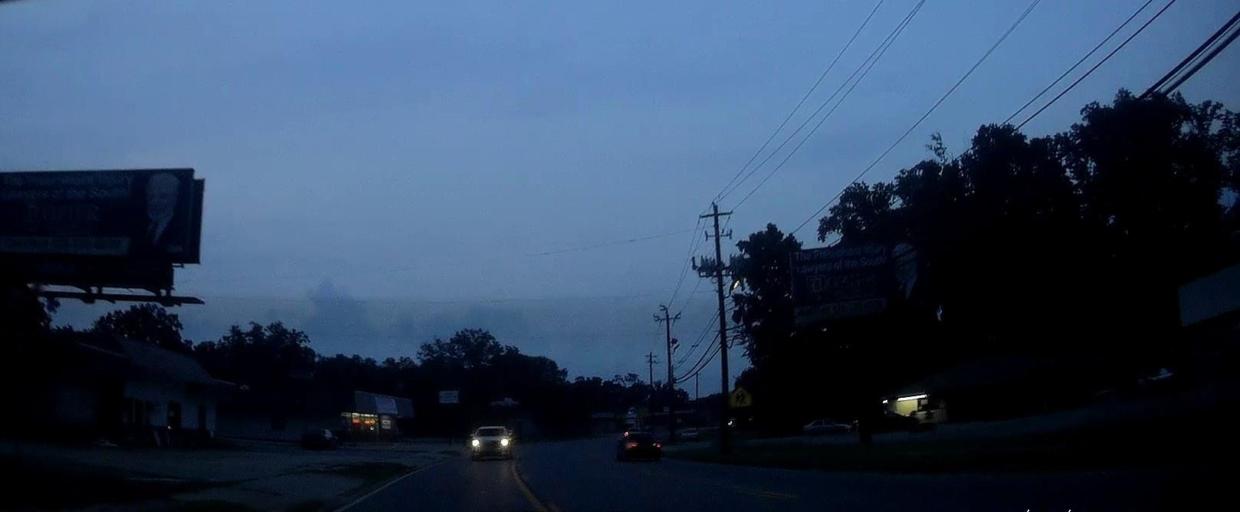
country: US
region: Georgia
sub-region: Laurens County
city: Dublin
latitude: 32.5328
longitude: -82.9117
